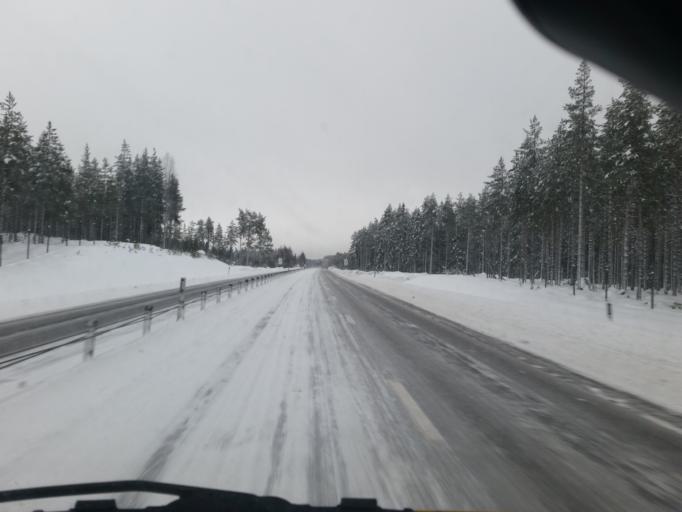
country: SE
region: Norrbotten
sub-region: Pitea Kommun
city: Pitea
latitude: 65.2742
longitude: 21.4527
